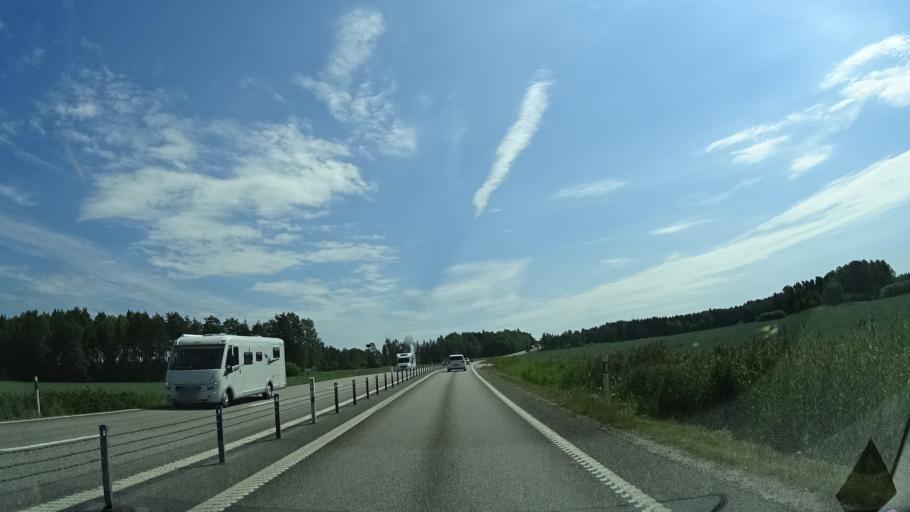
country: SE
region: Vaermland
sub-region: Kristinehamns Kommun
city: Kristinehamn
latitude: 59.3733
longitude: 13.9989
